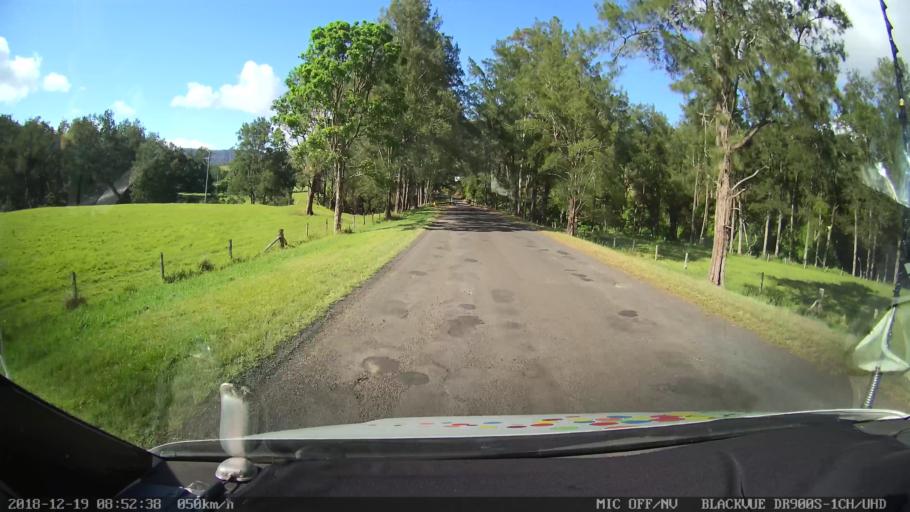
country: AU
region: New South Wales
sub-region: Kyogle
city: Kyogle
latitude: -28.3964
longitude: 152.9768
